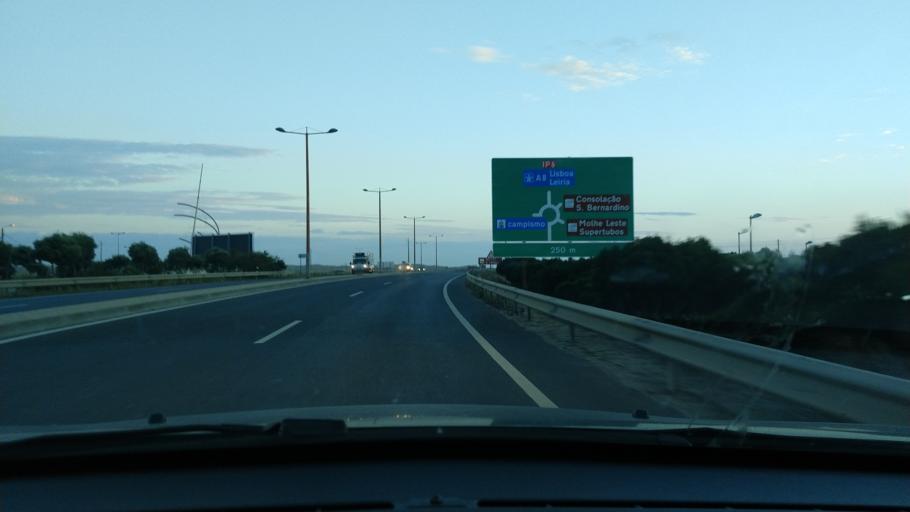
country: PT
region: Leiria
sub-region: Peniche
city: Peniche
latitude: 39.3523
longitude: -9.3615
